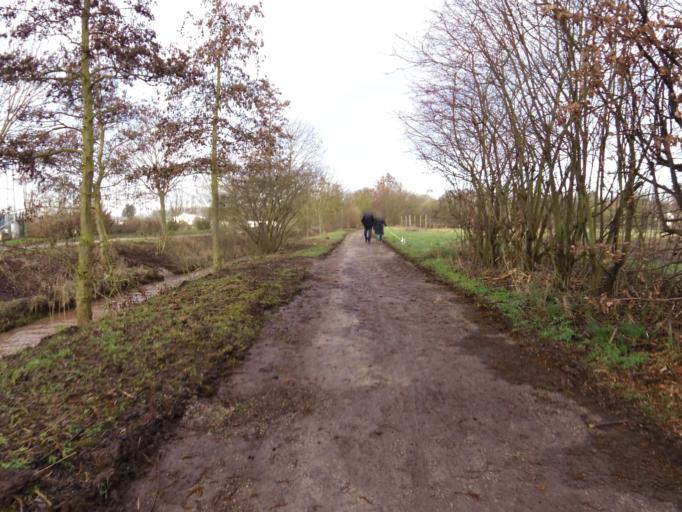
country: DE
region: Rheinland-Pfalz
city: Kleinniedesheim
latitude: 49.6072
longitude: 8.3203
